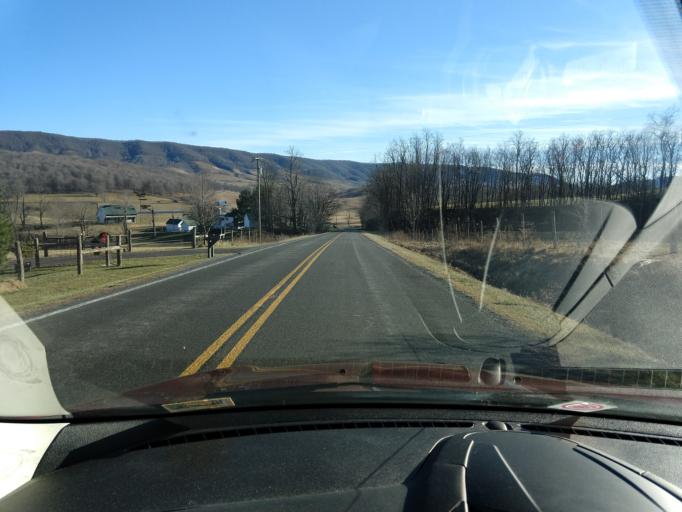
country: US
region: Virginia
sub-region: Highland County
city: Monterey
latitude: 38.4374
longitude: -79.6390
